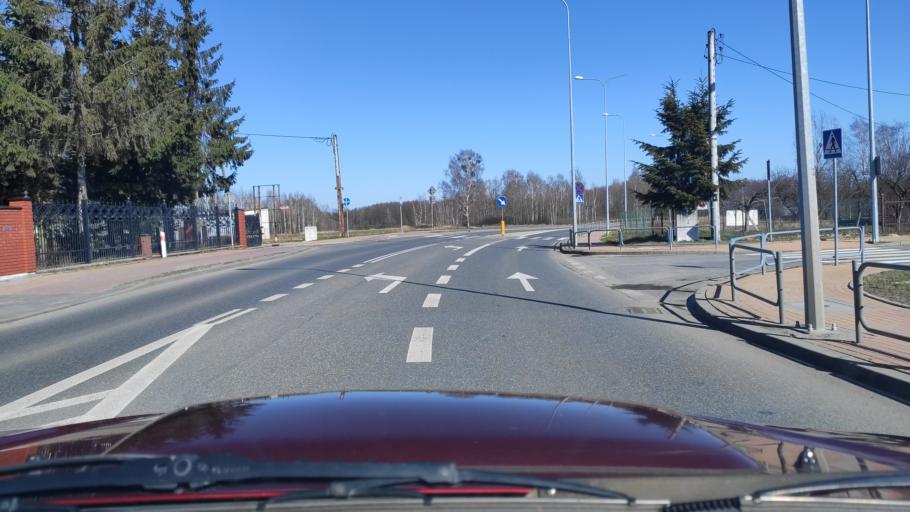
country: PL
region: Masovian Voivodeship
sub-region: Powiat zwolenski
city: Zwolen
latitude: 51.3719
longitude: 21.5870
